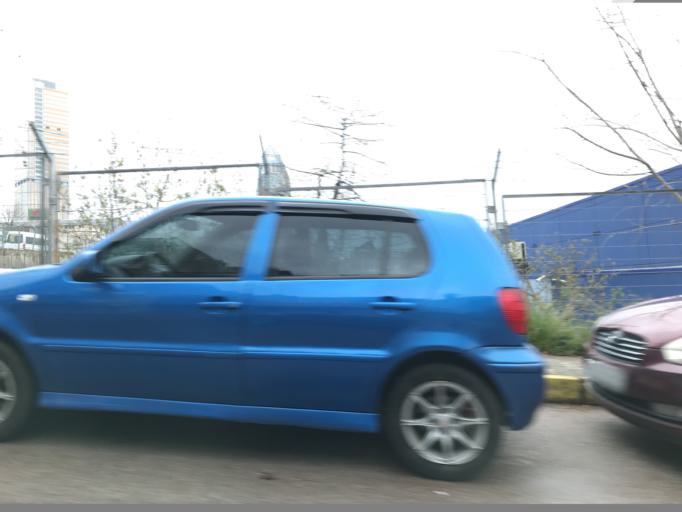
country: TR
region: Istanbul
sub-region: Atasehir
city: Atasehir
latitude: 40.9859
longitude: 29.0942
